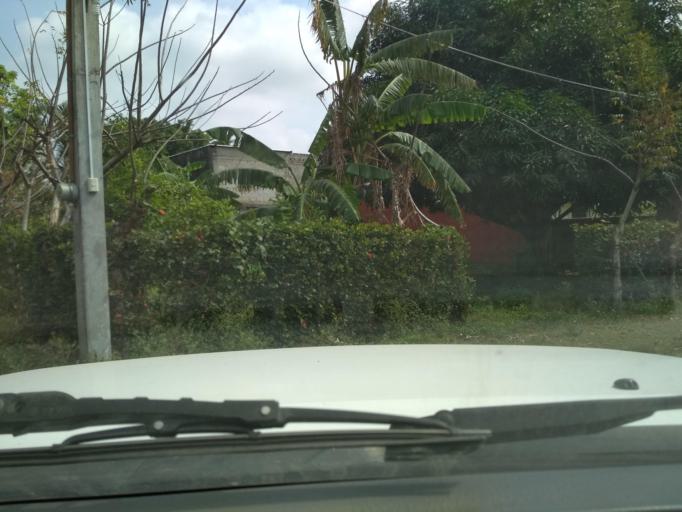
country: MX
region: Veracruz
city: El Tejar
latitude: 19.0794
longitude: -96.1699
